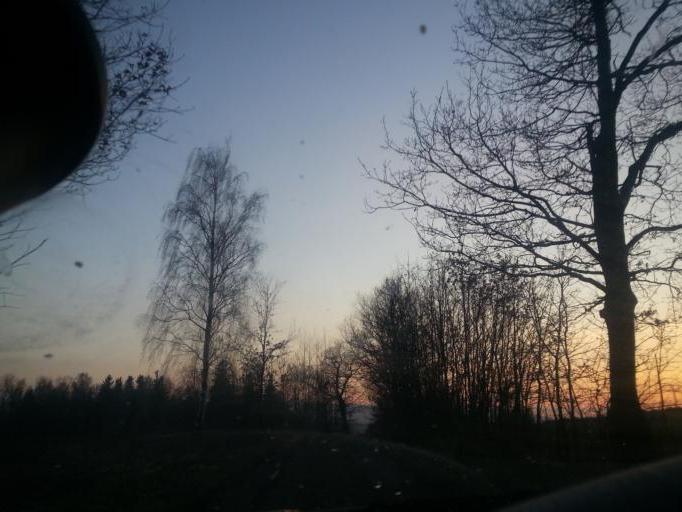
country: PL
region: Lower Silesian Voivodeship
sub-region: Powiat jeleniogorski
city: Stara Kamienica
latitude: 50.9645
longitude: 15.6028
